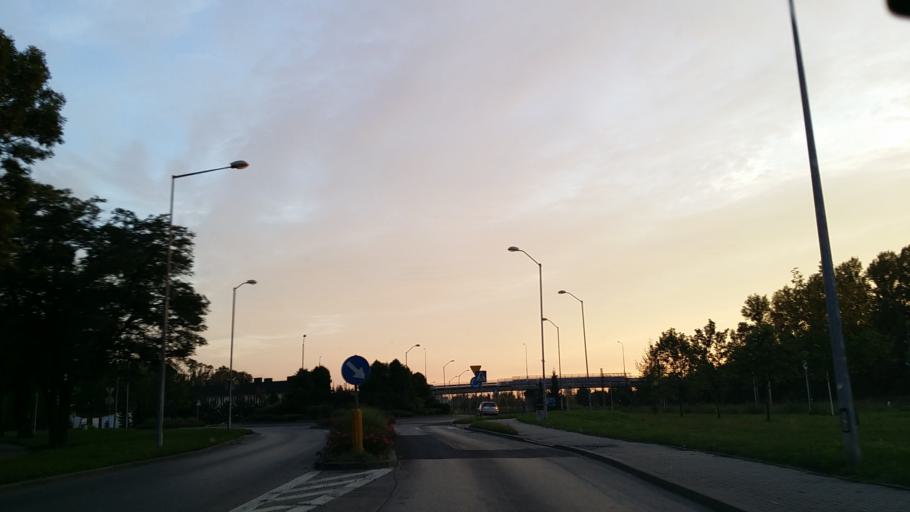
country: PL
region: Lesser Poland Voivodeship
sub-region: Powiat oswiecimski
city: Brzezinka
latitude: 50.0376
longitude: 19.1956
